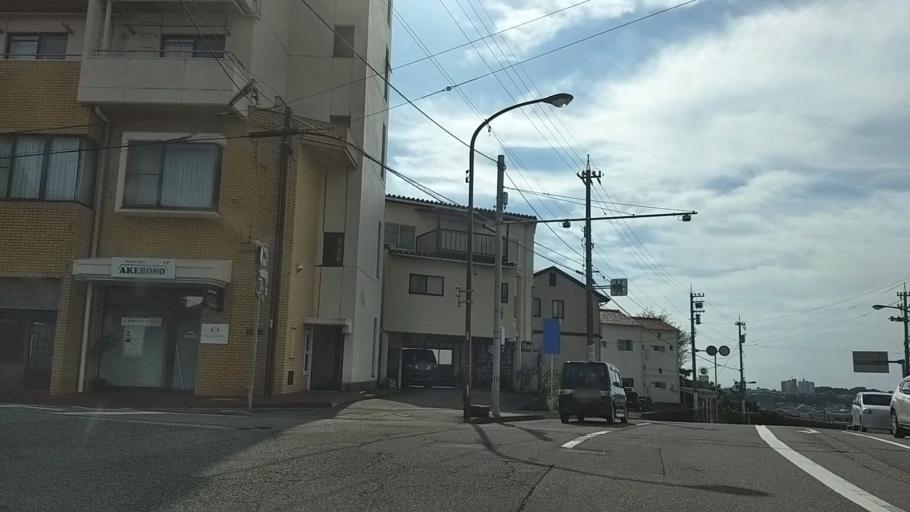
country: JP
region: Ishikawa
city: Nonoichi
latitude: 36.5526
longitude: 136.6735
